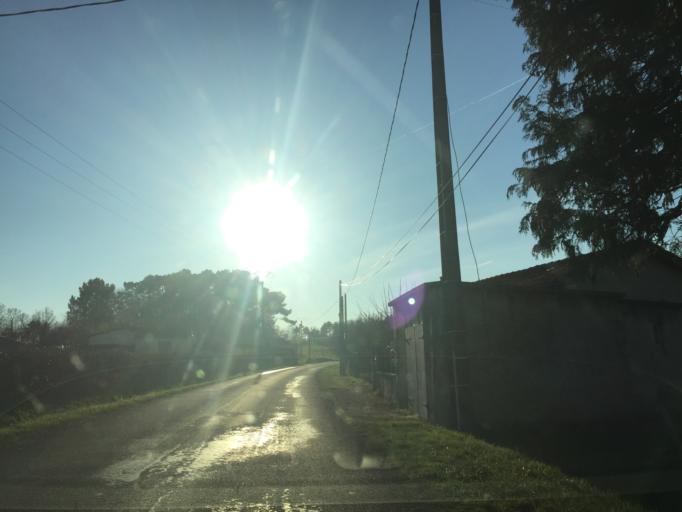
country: FR
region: Aquitaine
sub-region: Departement de la Dordogne
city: Riberac
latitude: 45.2001
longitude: 0.3443
